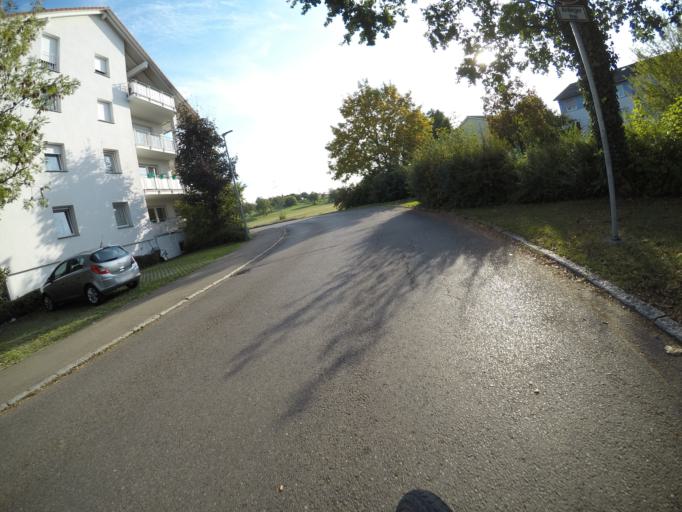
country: DE
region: Baden-Wuerttemberg
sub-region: Tuebingen Region
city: Sickenhausen
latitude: 48.5253
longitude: 9.1978
